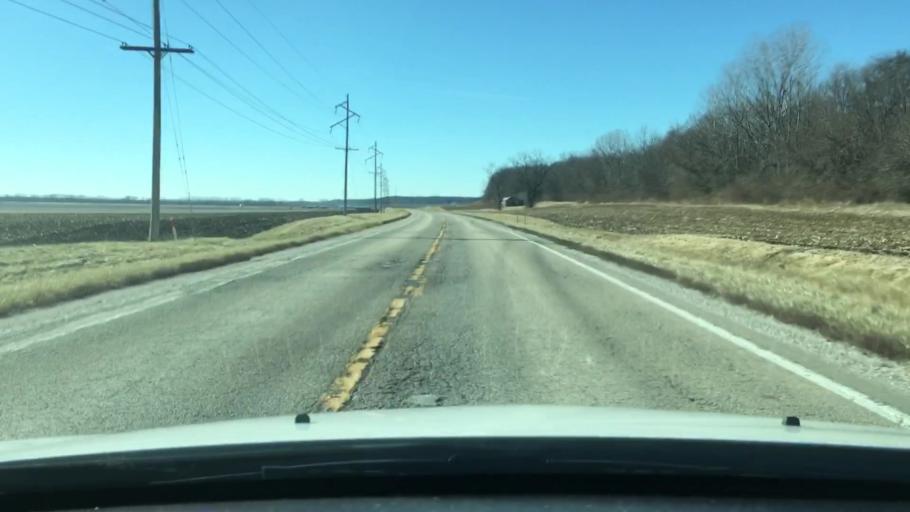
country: US
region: Illinois
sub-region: Fulton County
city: Astoria
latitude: 40.1777
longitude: -90.2508
